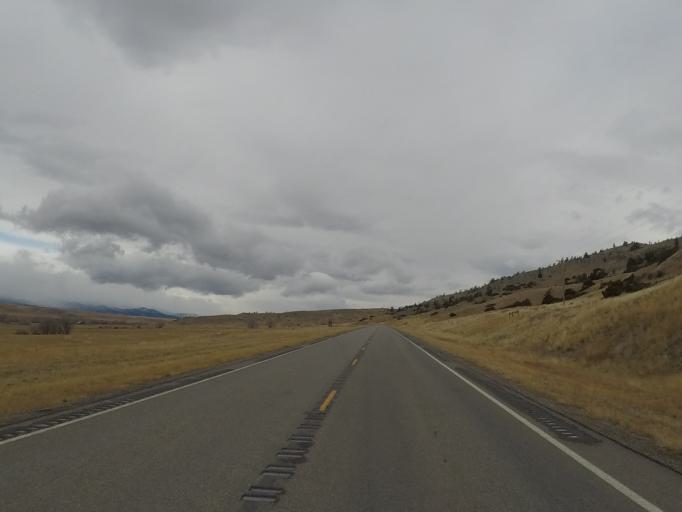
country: US
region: Montana
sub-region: Sweet Grass County
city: Big Timber
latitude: 45.8898
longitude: -109.9598
